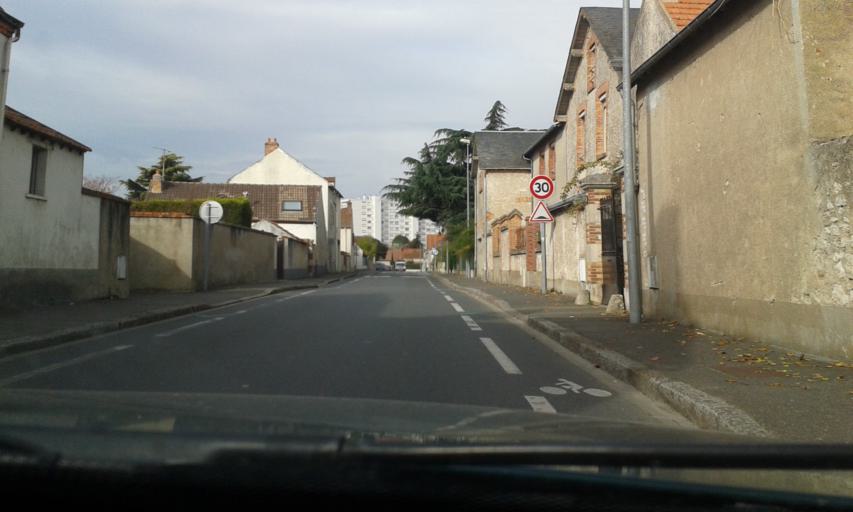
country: FR
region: Centre
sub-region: Departement du Loiret
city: Saint-Jean-le-Blanc
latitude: 47.8786
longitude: 1.9121
